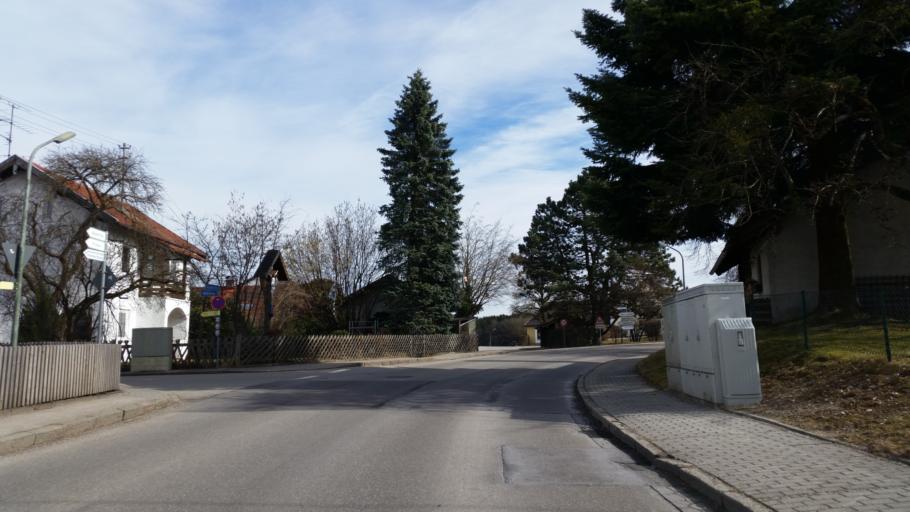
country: DE
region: Bavaria
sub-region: Upper Bavaria
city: Oberpframmern
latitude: 48.0209
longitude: 11.8166
